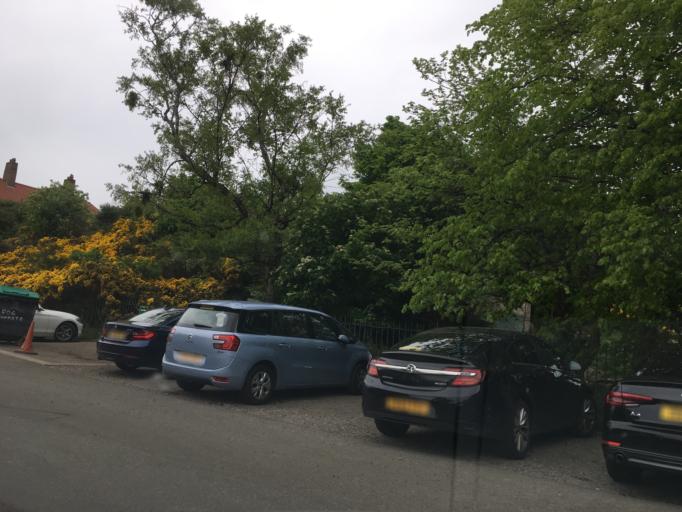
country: GB
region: Scotland
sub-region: Edinburgh
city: Edinburgh
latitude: 55.9151
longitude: -3.2047
